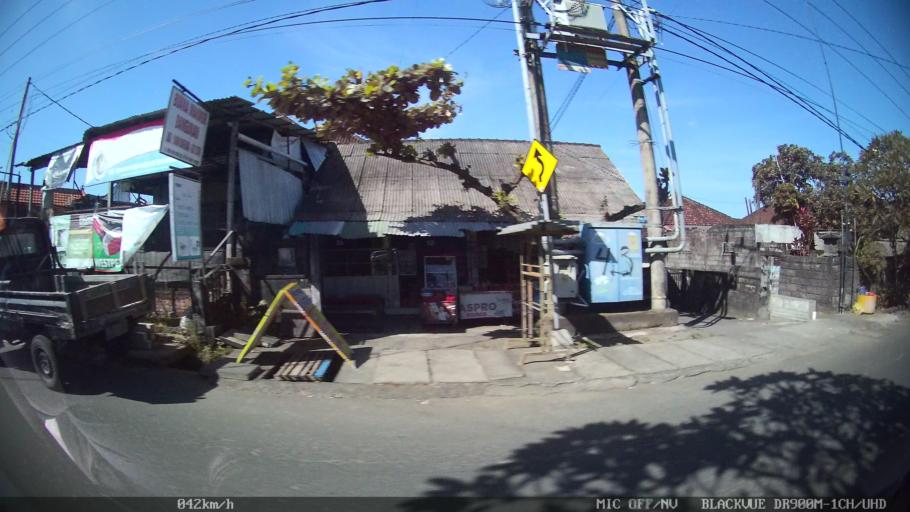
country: ID
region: Bali
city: Banjar Kertasari
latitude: -8.6230
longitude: 115.1852
